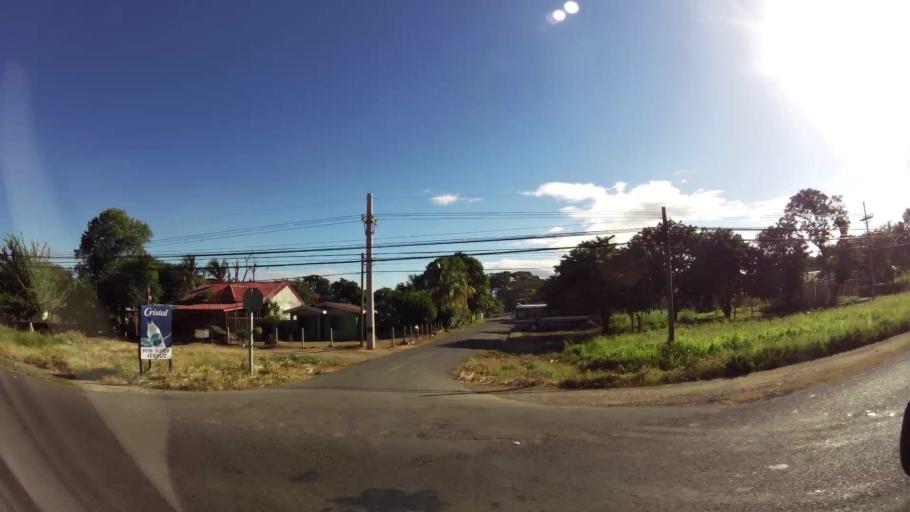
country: CR
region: Guanacaste
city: Belen
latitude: 10.4572
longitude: -85.5567
